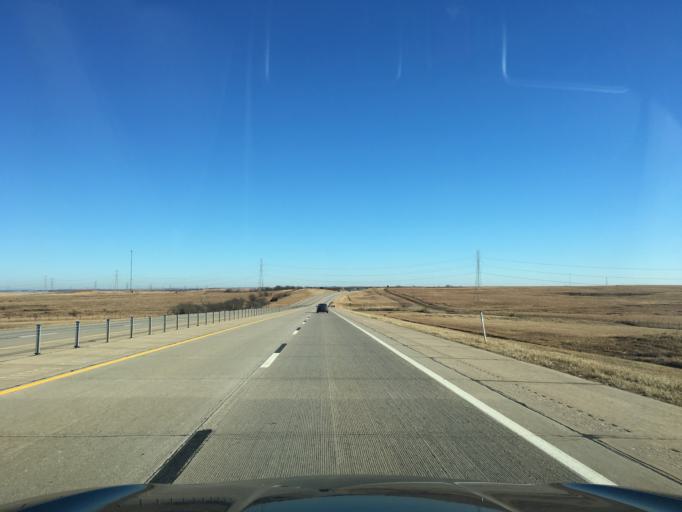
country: US
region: Oklahoma
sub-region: Noble County
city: Perry
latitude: 36.3921
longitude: -97.1151
